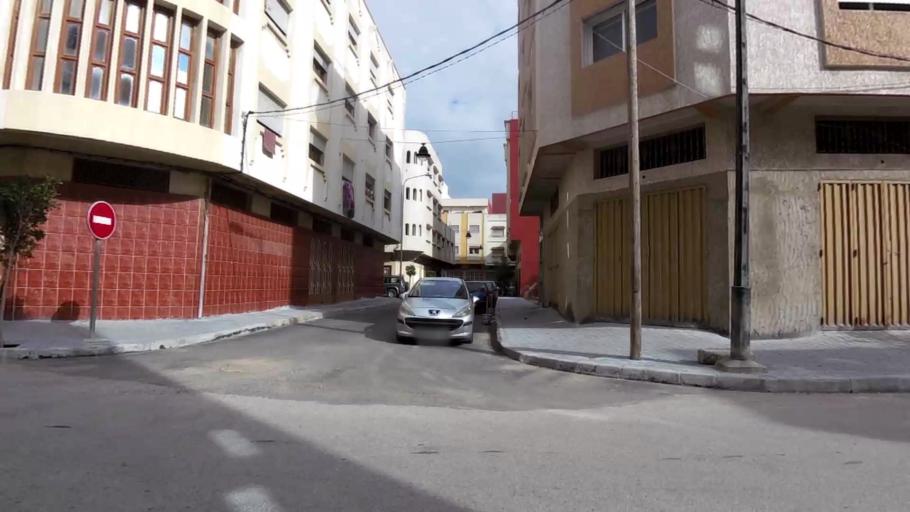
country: MA
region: Tanger-Tetouan
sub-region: Tanger-Assilah
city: Tangier
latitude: 35.7547
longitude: -5.7945
